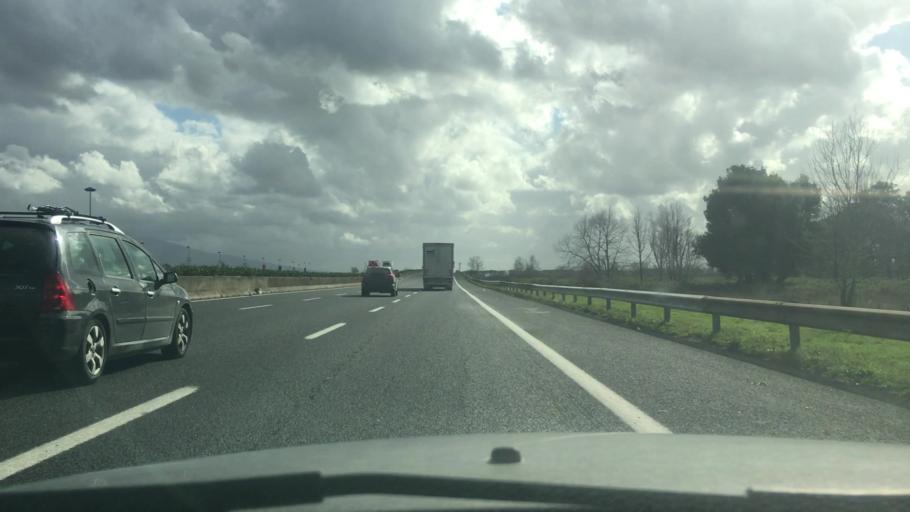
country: IT
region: Campania
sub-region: Provincia di Napoli
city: Pascarola
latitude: 41.0048
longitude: 14.3234
